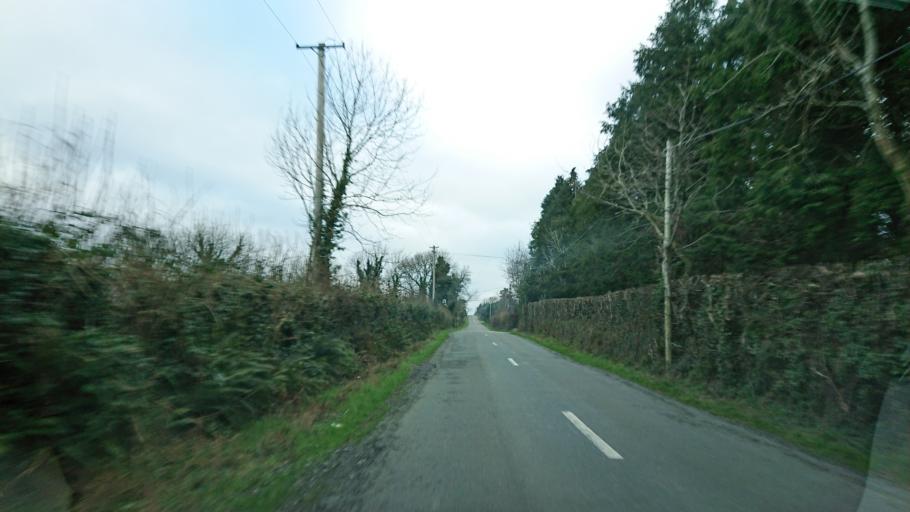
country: IE
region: Munster
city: Carrick-on-Suir
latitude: 52.3190
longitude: -7.5552
